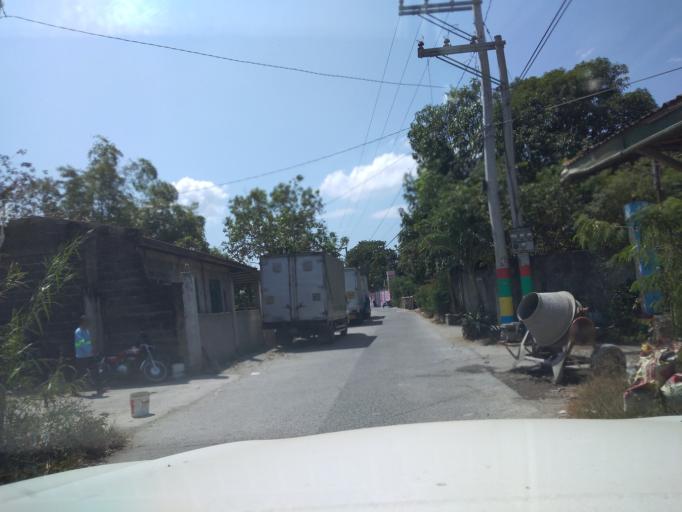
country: PH
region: Central Luzon
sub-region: Province of Pampanga
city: Lourdes
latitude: 15.0141
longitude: 120.8454
